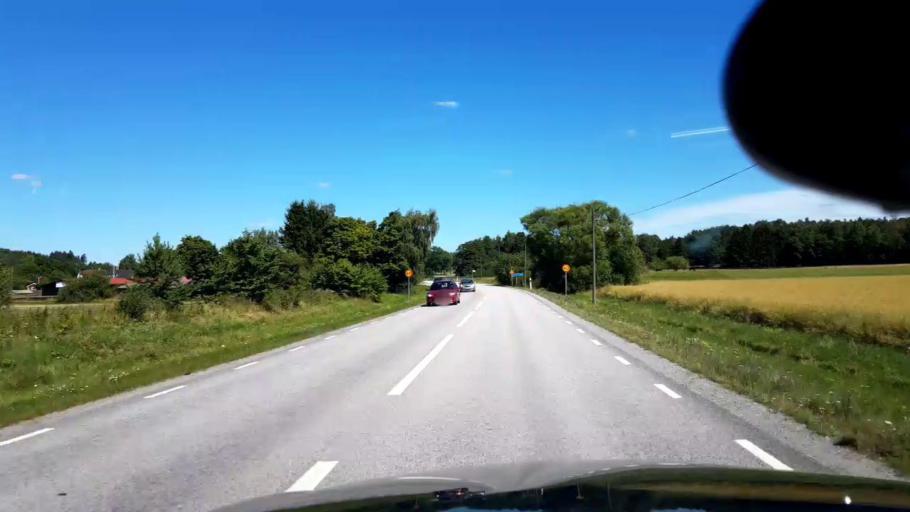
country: SE
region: Uppsala
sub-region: Habo Kommun
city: Balsta
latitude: 59.6376
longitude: 17.6081
